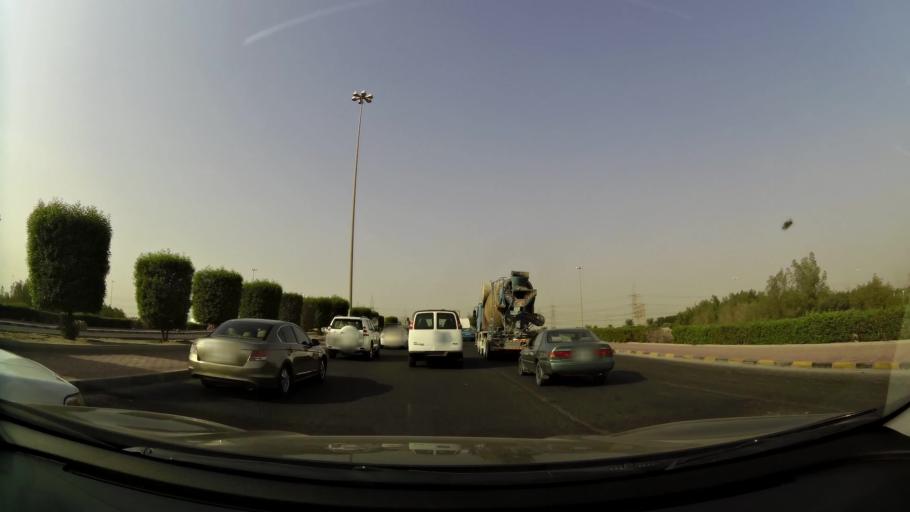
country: KW
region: Mubarak al Kabir
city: Mubarak al Kabir
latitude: 29.1771
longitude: 48.0711
